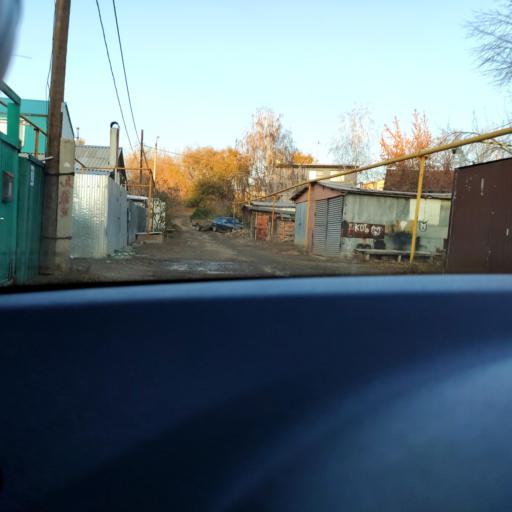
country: RU
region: Samara
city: Samara
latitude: 53.1934
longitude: 50.1545
